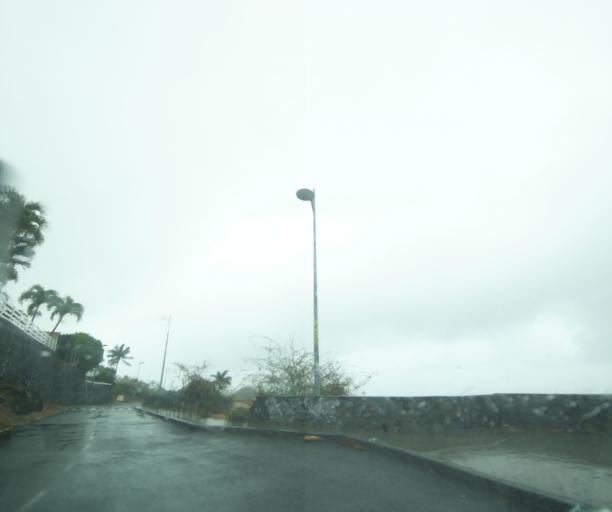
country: RE
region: Reunion
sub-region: Reunion
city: Saint-Paul
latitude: -21.0459
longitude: 55.2255
